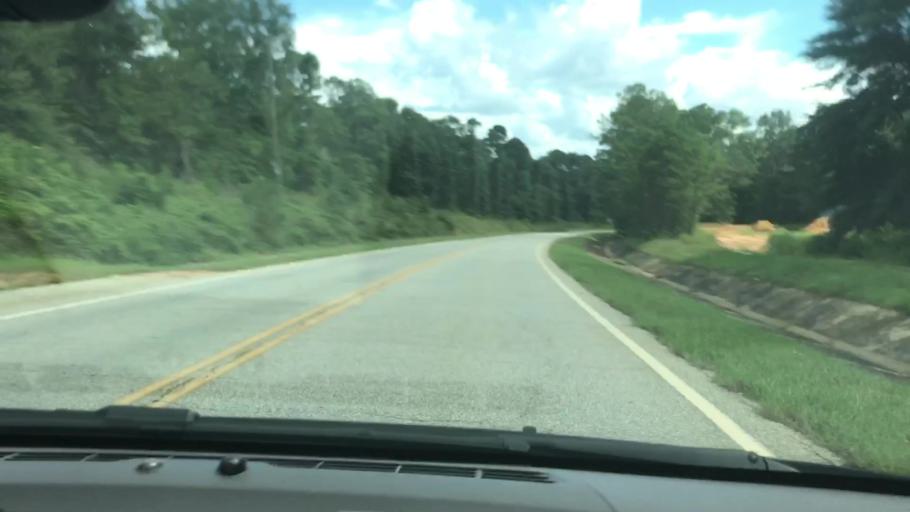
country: US
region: Georgia
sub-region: Quitman County
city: Georgetown
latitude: 31.7542
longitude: -85.0588
